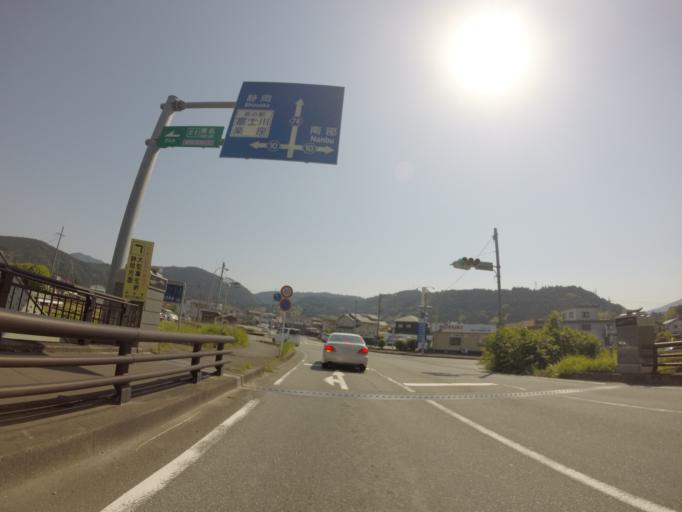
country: JP
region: Shizuoka
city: Fujinomiya
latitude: 35.1934
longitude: 138.5895
